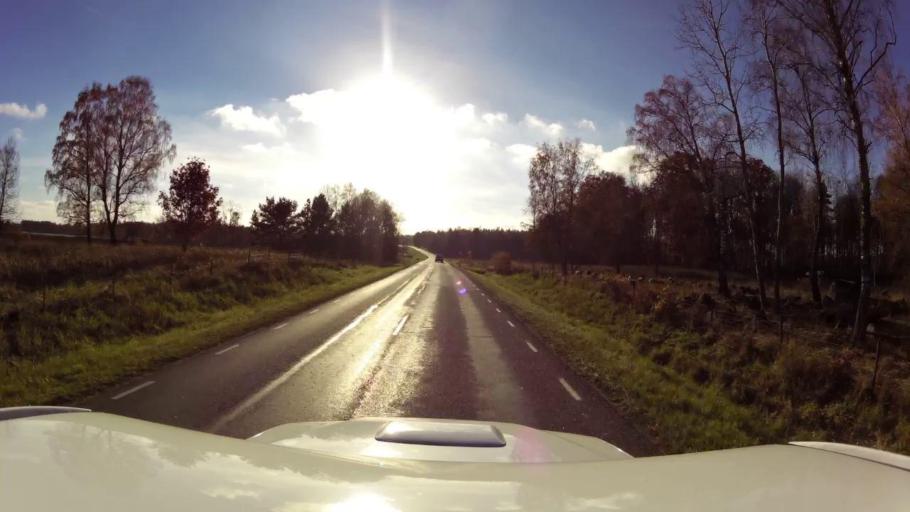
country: SE
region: OEstergoetland
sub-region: Linkopings Kommun
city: Malmslatt
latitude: 58.3433
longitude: 15.5192
